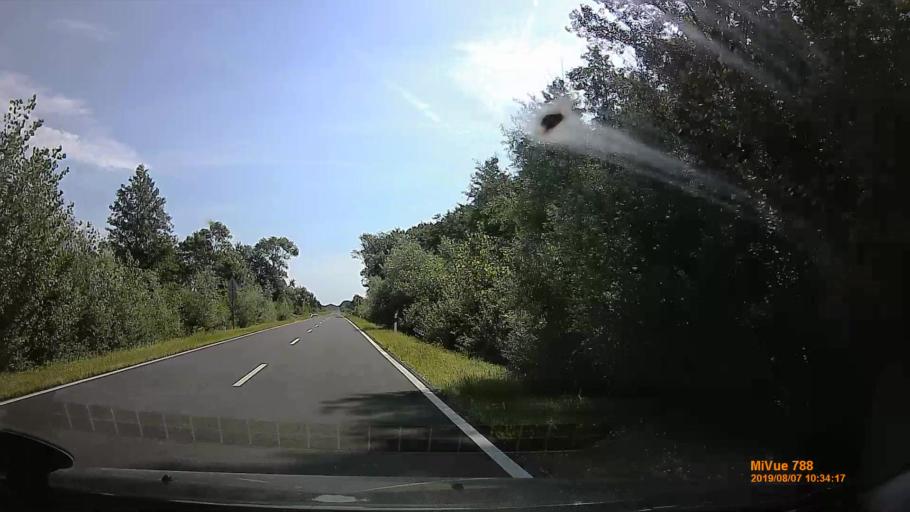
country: SI
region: Lendava-Lendva
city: Lendava
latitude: 46.6170
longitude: 16.4242
